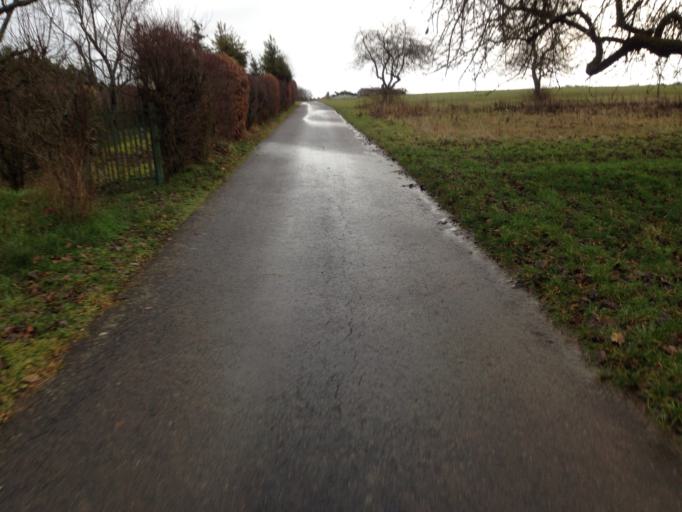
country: DE
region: Baden-Wuerttemberg
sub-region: Karlsruhe Region
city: Limbach
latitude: 49.4044
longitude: 9.2225
